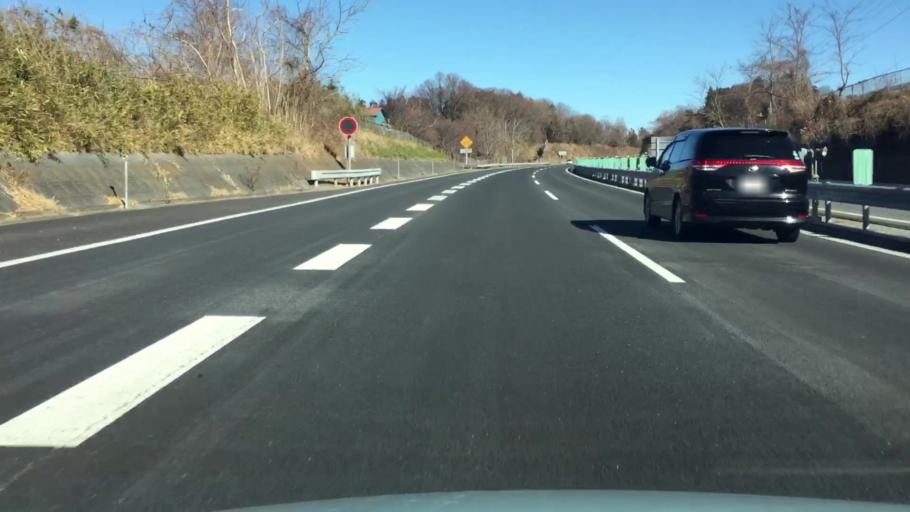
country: JP
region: Gunma
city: Shibukawa
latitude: 36.5237
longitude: 139.0396
